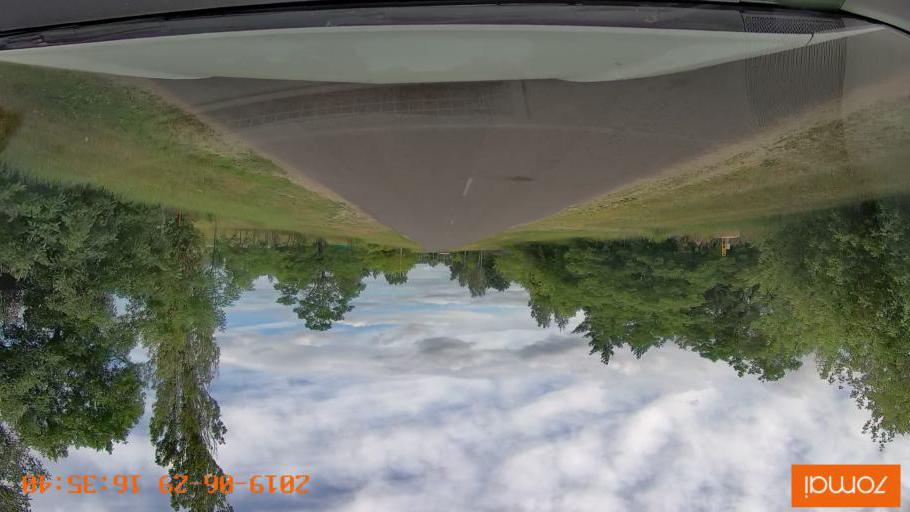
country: BY
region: Brest
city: Luninyets
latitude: 52.2145
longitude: 27.0178
